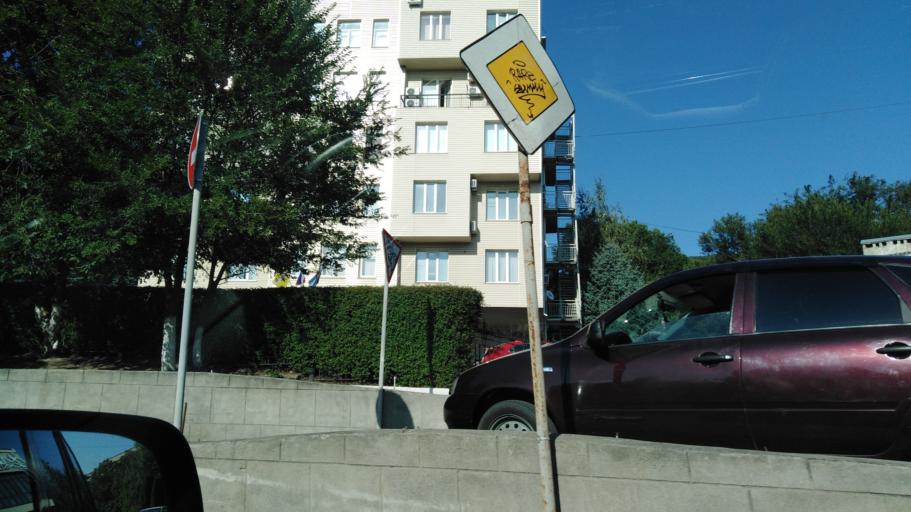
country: RU
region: Stavropol'skiy
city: Pyatigorsk
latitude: 44.0483
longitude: 43.0685
